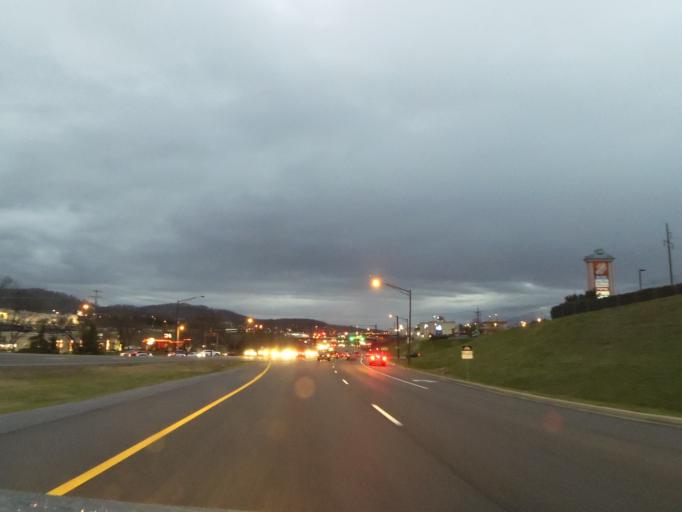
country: US
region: Tennessee
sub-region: Washington County
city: Midway
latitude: 36.3507
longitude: -82.4004
